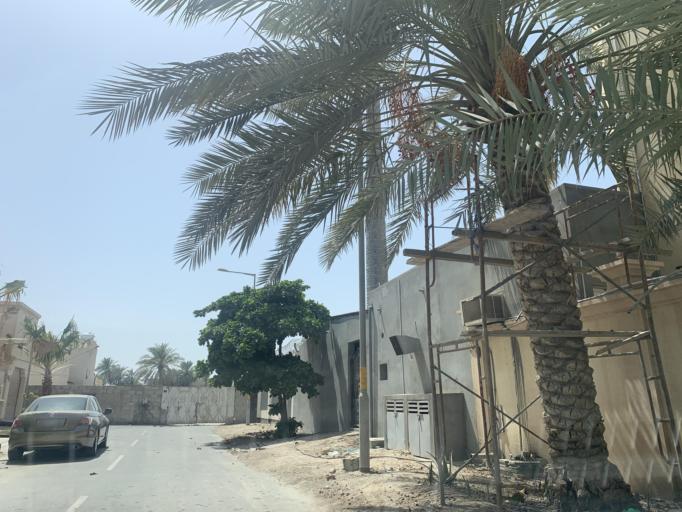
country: BH
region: Central Governorate
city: Madinat Hamad
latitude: 26.1499
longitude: 50.4990
